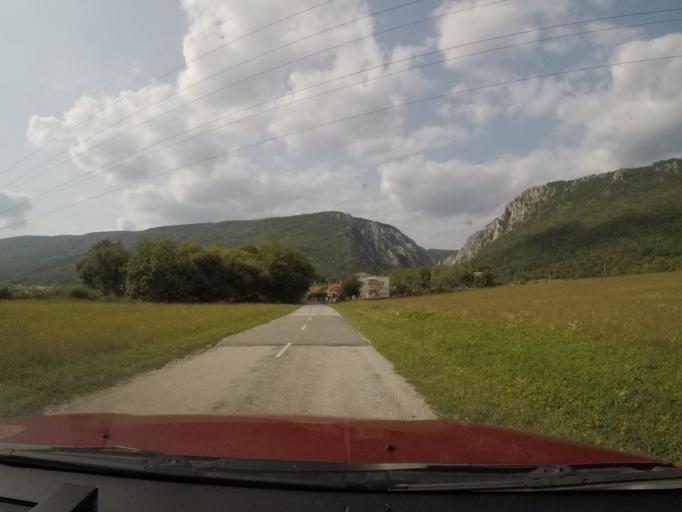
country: SK
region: Kosicky
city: Medzev
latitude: 48.6101
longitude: 20.8354
